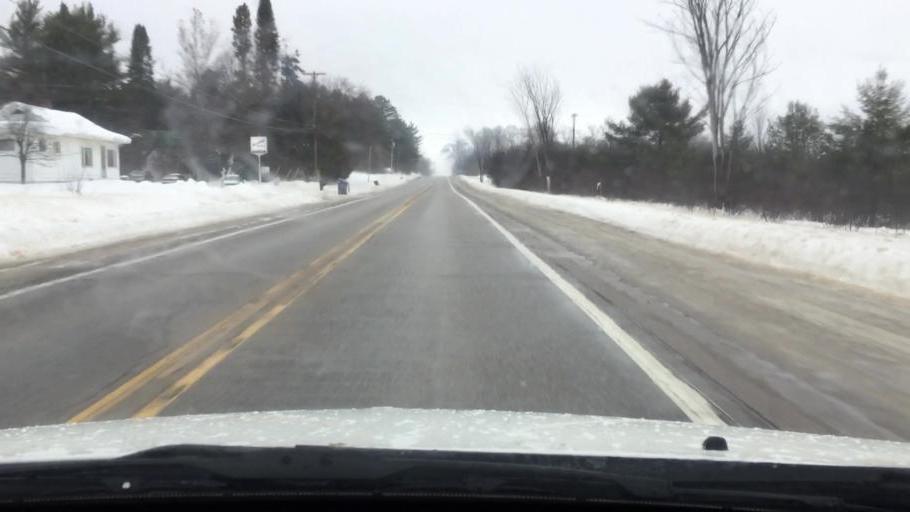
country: US
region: Michigan
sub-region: Charlevoix County
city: East Jordan
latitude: 45.1403
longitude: -85.1398
